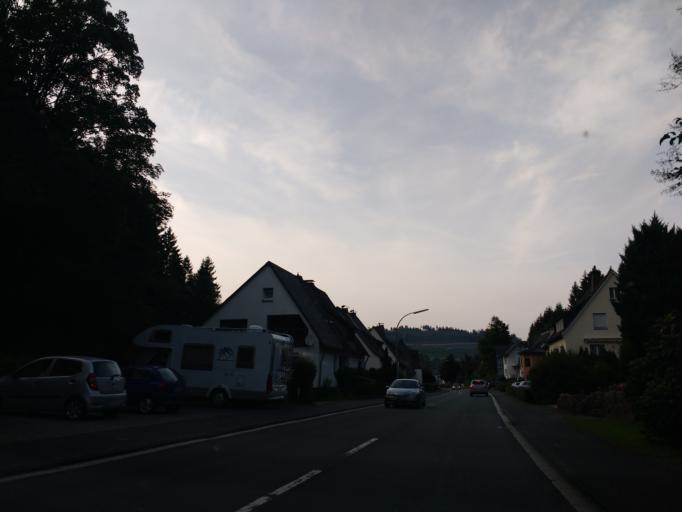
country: DE
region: North Rhine-Westphalia
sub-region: Regierungsbezirk Arnsberg
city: Bestwig
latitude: 51.3570
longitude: 8.4192
